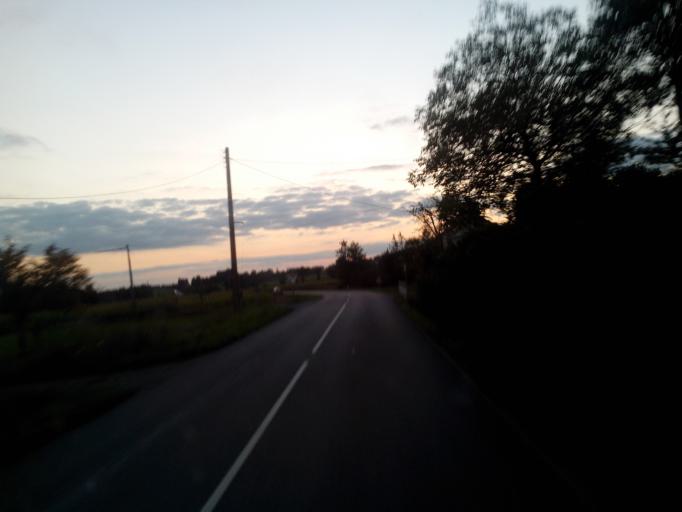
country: FR
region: Brittany
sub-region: Departement d'Ille-et-Vilaine
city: Montfort-sur-Meu
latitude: 48.1386
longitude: -1.9897
